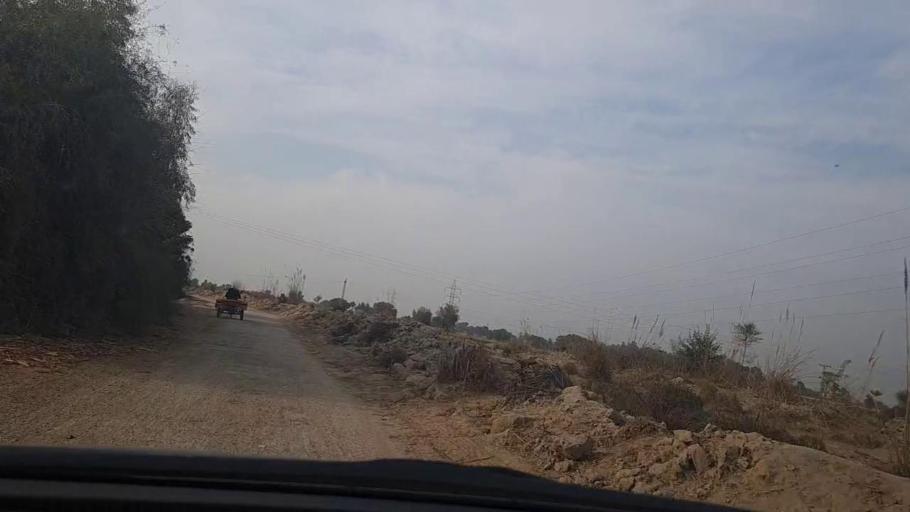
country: PK
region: Sindh
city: Daulatpur
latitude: 26.3332
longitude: 68.0769
